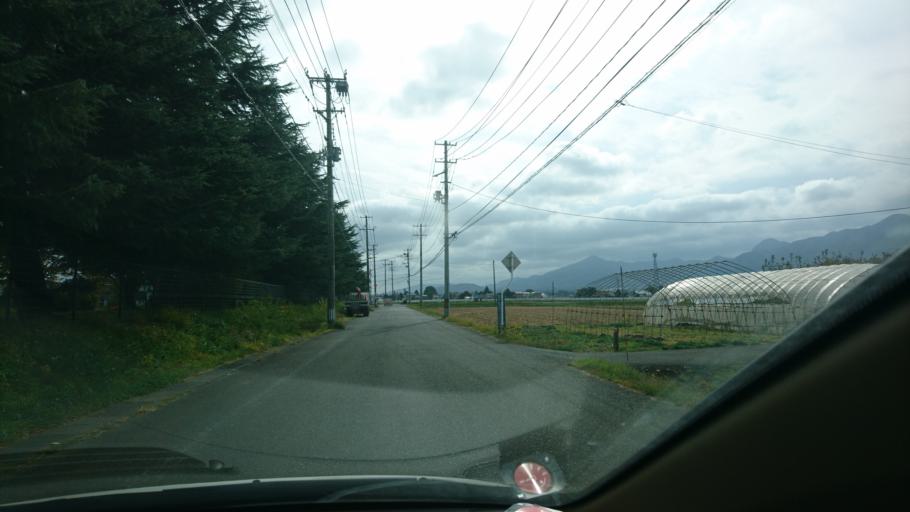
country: JP
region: Iwate
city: Morioka-shi
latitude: 39.6759
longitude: 141.1286
